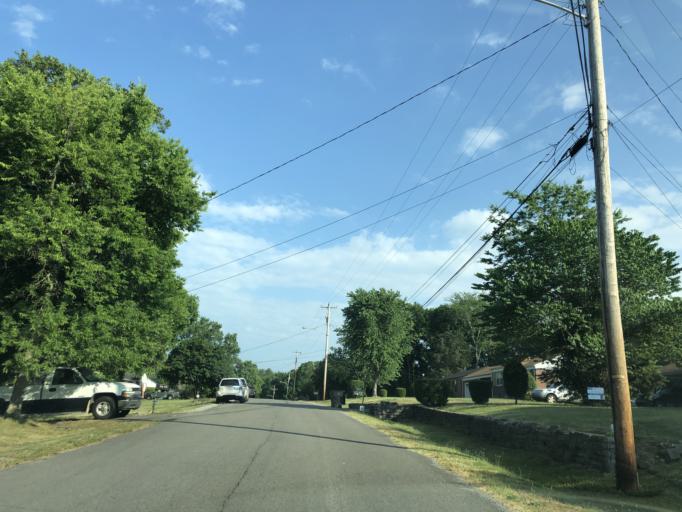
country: US
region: Tennessee
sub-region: Davidson County
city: Nashville
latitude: 36.2150
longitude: -86.8037
